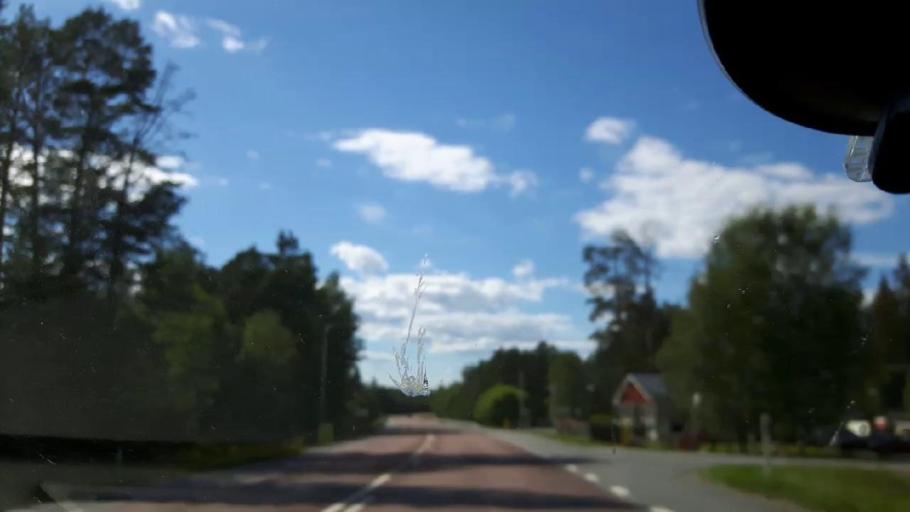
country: SE
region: Jaemtland
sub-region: Braecke Kommun
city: Braecke
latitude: 62.8146
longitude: 15.3536
